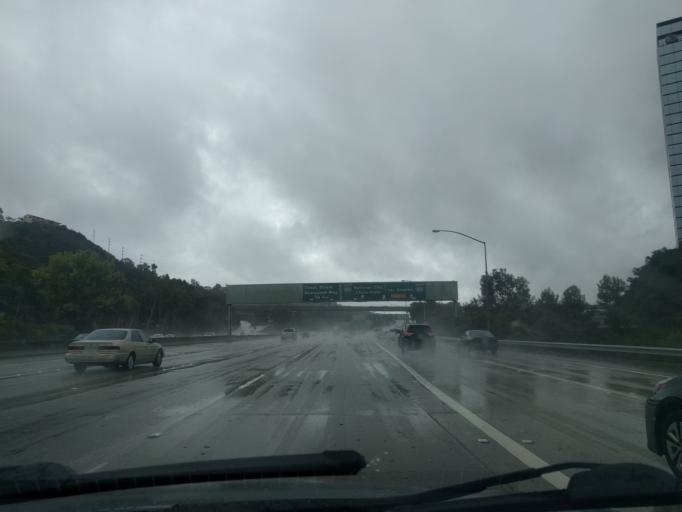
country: US
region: California
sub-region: San Diego County
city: San Diego
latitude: 32.7744
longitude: -117.1260
